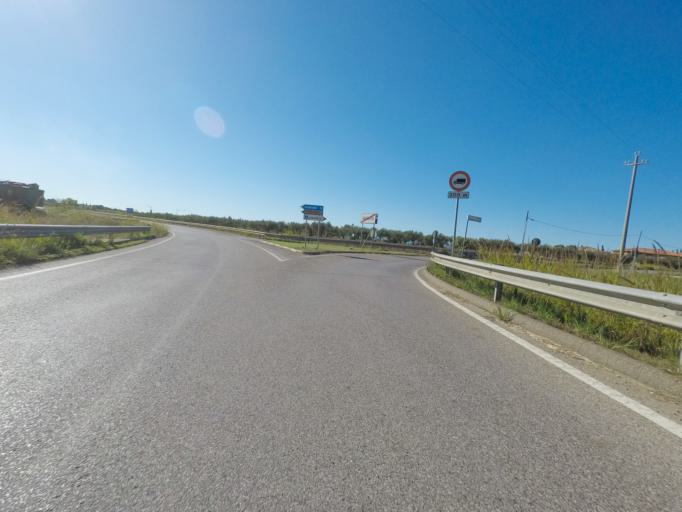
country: IT
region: Tuscany
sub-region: Provincia di Grosseto
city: Grosseto
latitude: 42.7680
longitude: 11.1430
